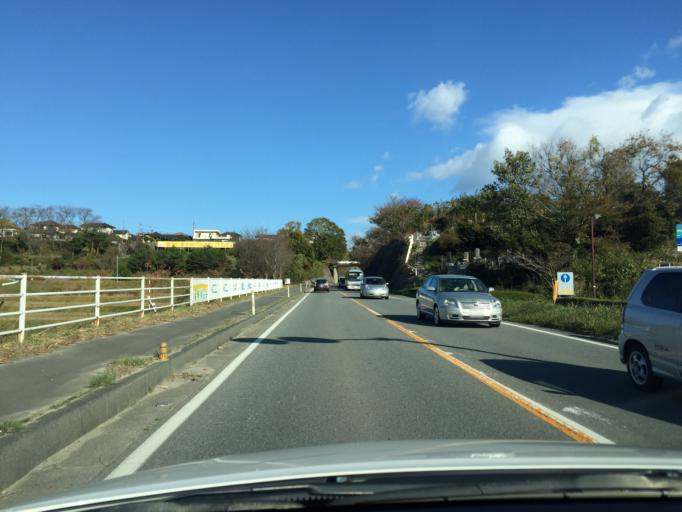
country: JP
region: Fukushima
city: Iwaki
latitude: 37.2087
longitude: 140.9932
